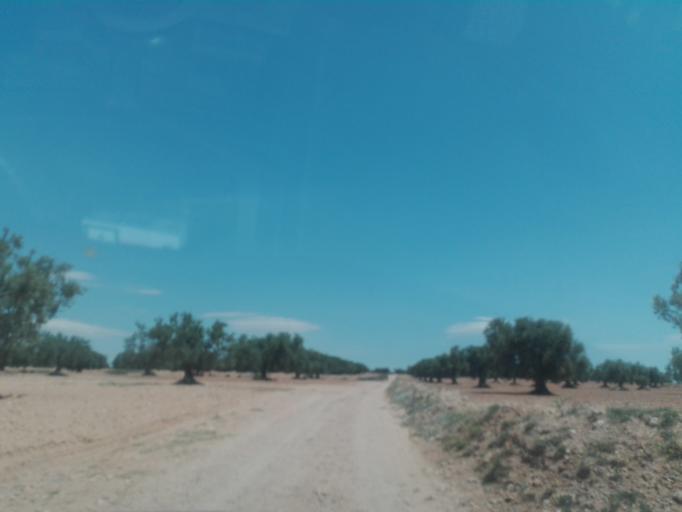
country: TN
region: Safaqis
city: Sfax
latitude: 34.6618
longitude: 10.6037
